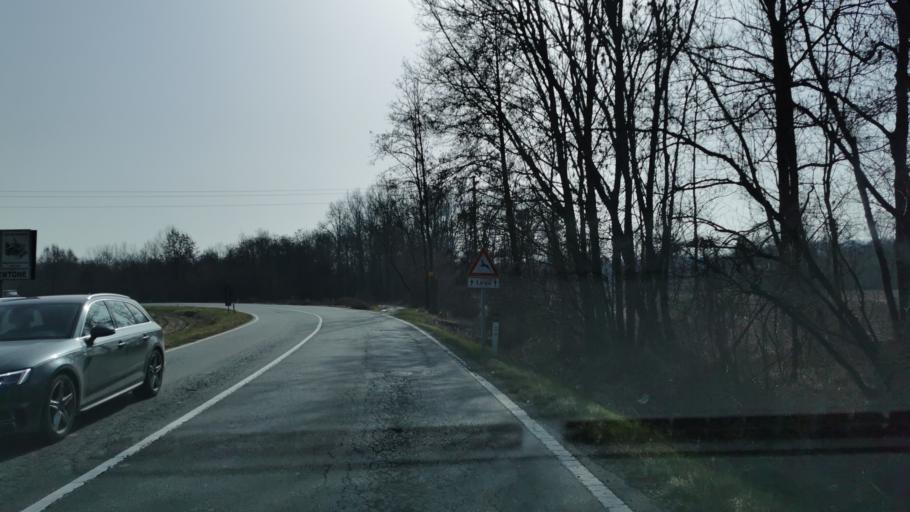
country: IT
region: Piedmont
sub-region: Provincia di Torino
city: San Benigno Canavese
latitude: 45.2212
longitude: 7.7617
